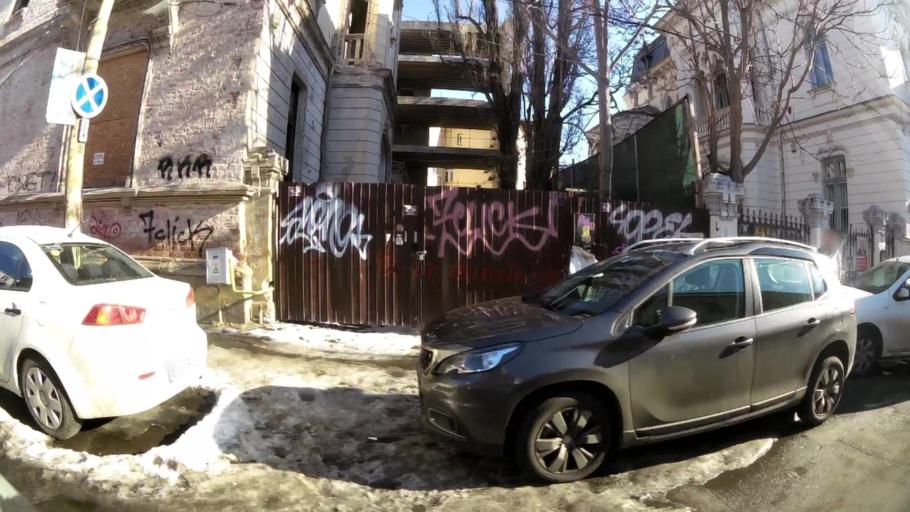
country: RO
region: Bucuresti
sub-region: Municipiul Bucuresti
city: Bucharest
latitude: 44.4404
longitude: 26.1047
